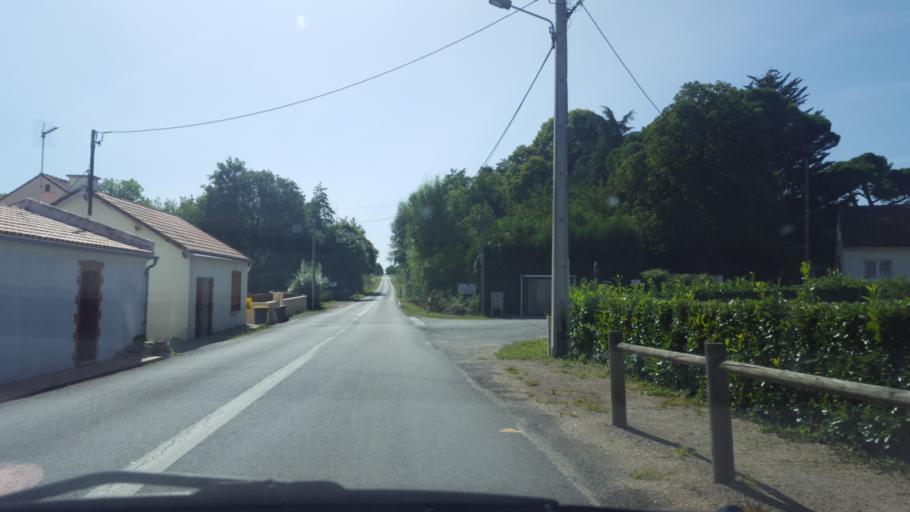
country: FR
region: Pays de la Loire
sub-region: Departement de la Loire-Atlantique
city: La Limouziniere
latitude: 46.9893
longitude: -1.6136
